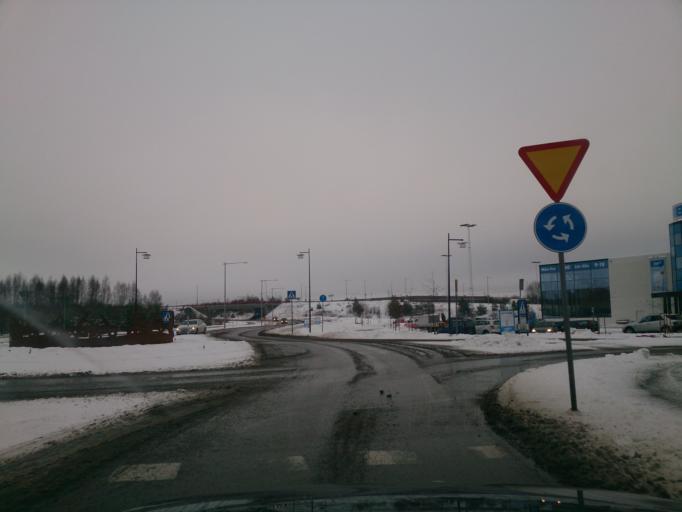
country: SE
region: OEstergoetland
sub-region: Norrkopings Kommun
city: Norrkoping
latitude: 58.6245
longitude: 16.1543
